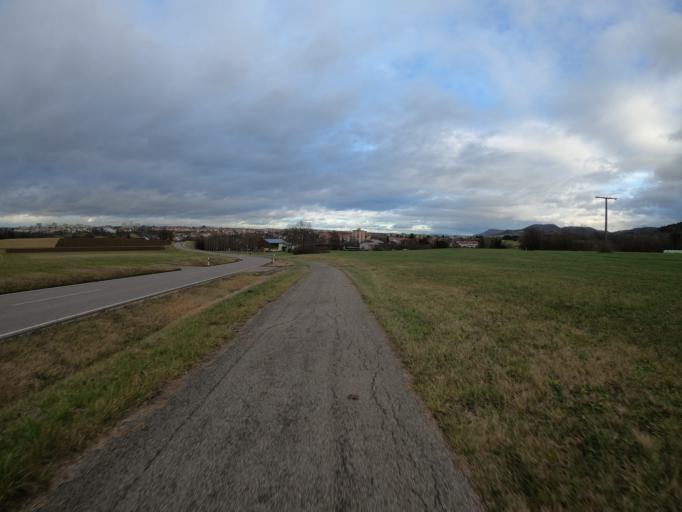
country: DE
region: Baden-Wuerttemberg
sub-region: Regierungsbezirk Stuttgart
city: Waldstetten
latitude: 48.7764
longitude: 9.8371
